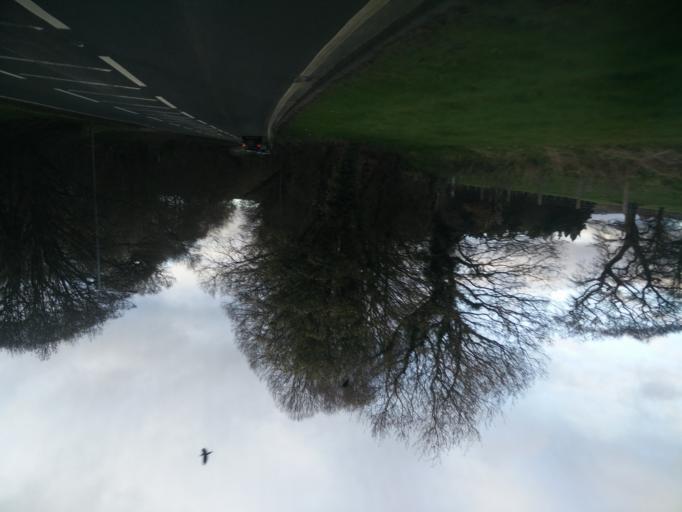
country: GB
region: England
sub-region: County Durham
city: Ushaw Moor
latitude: 54.7324
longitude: -1.6578
